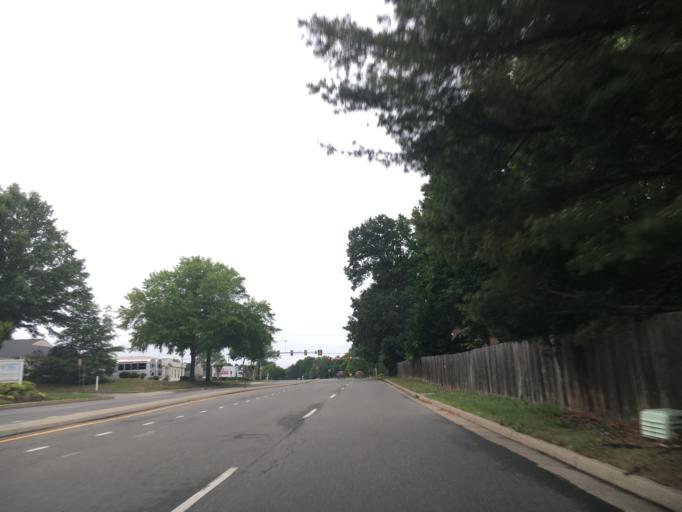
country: US
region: Virginia
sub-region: Henrico County
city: Short Pump
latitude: 37.6237
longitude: -77.6362
